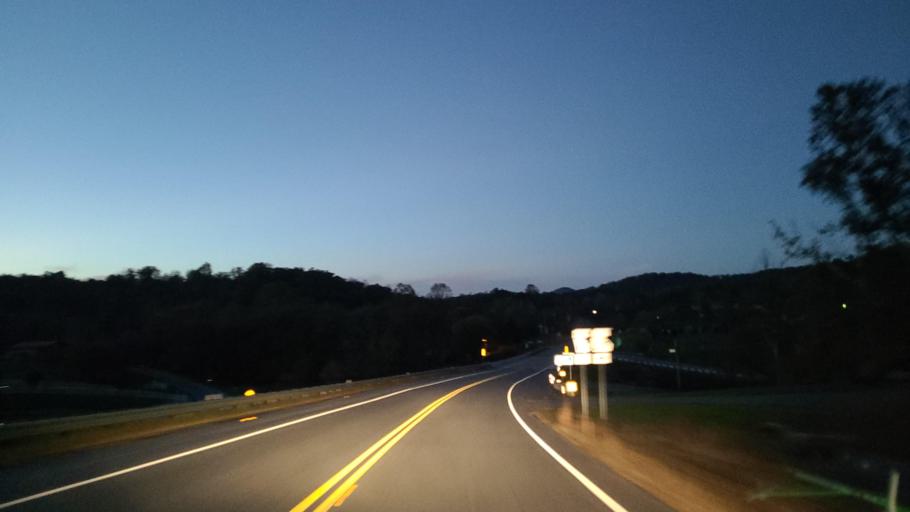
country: US
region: North Carolina
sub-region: Clay County
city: Hayesville
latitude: 34.9724
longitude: -83.8818
